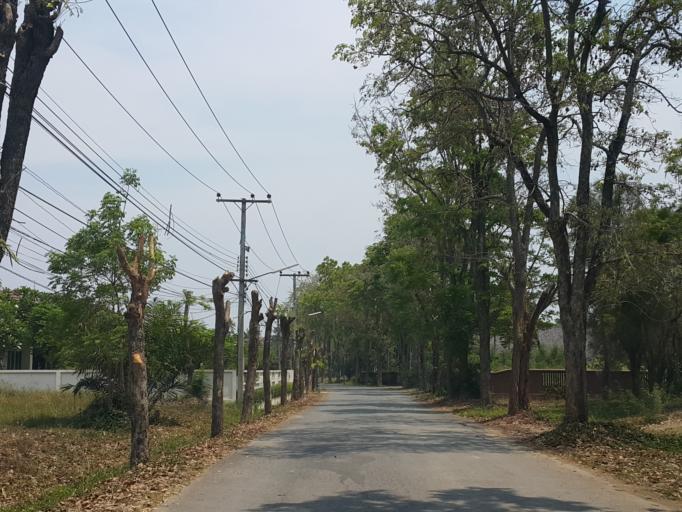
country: TH
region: Chiang Mai
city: Chiang Mai
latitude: 18.7332
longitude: 98.9749
